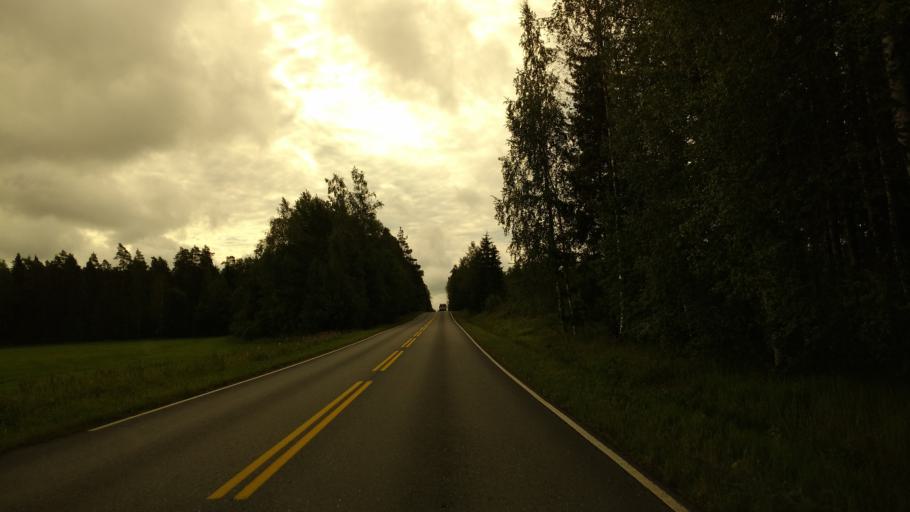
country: FI
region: Varsinais-Suomi
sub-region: Salo
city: Kuusjoki
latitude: 60.5626
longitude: 23.1506
